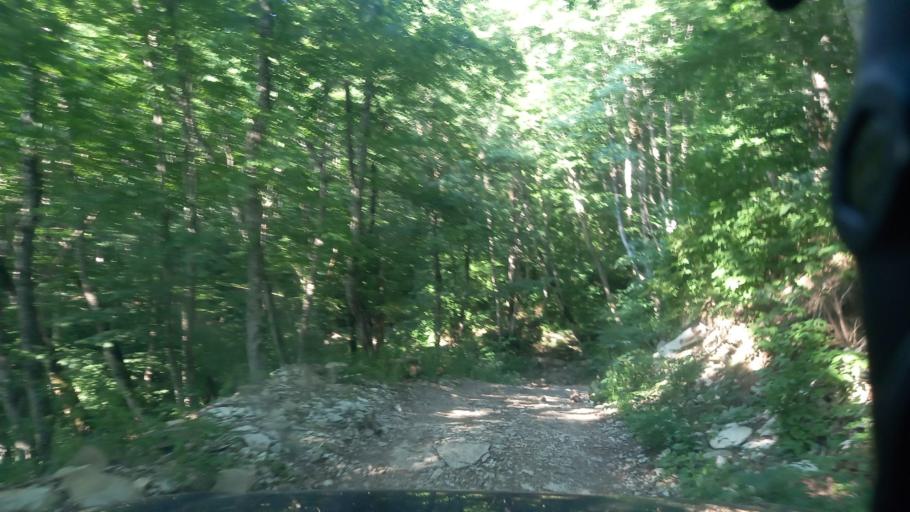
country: RU
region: Krasnodarskiy
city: Pshada
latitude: 44.5947
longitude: 38.2811
